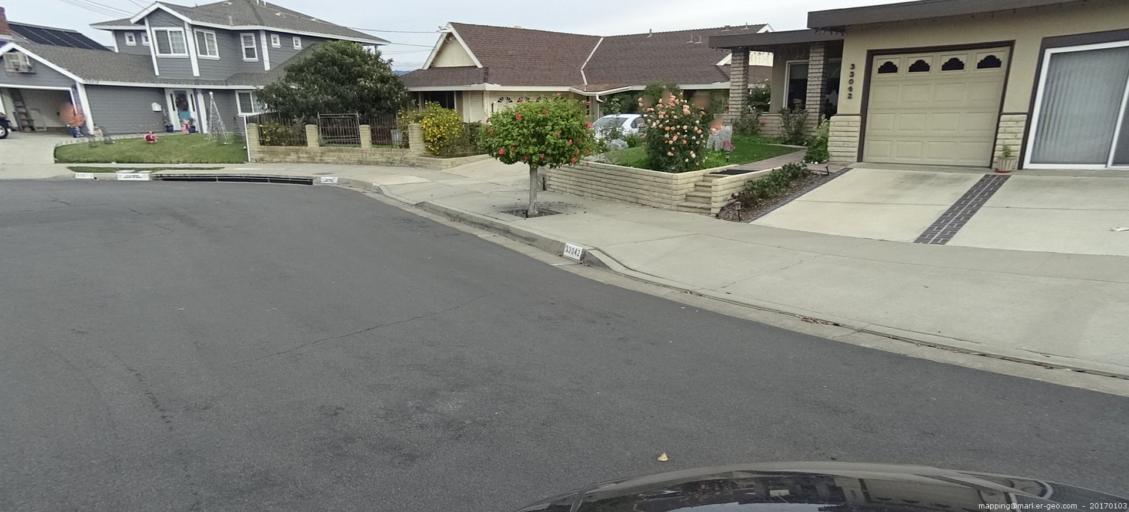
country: US
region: California
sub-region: Orange County
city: Dana Point
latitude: 33.4831
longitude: -117.6856
